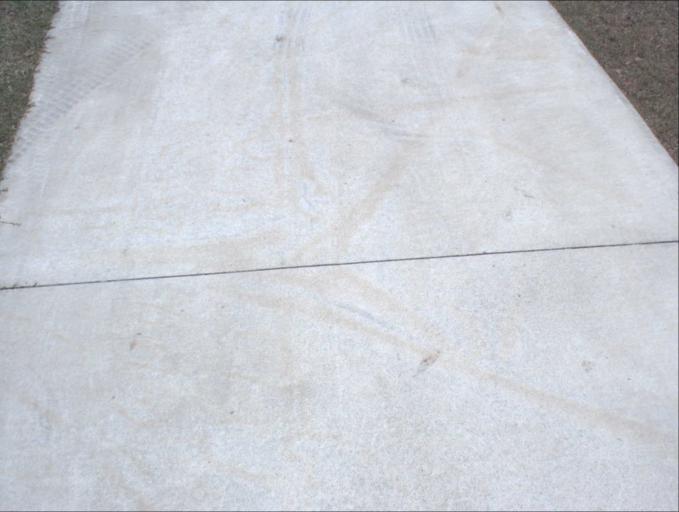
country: AU
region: Queensland
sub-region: Logan
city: North Maclean
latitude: -27.8123
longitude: 152.9605
